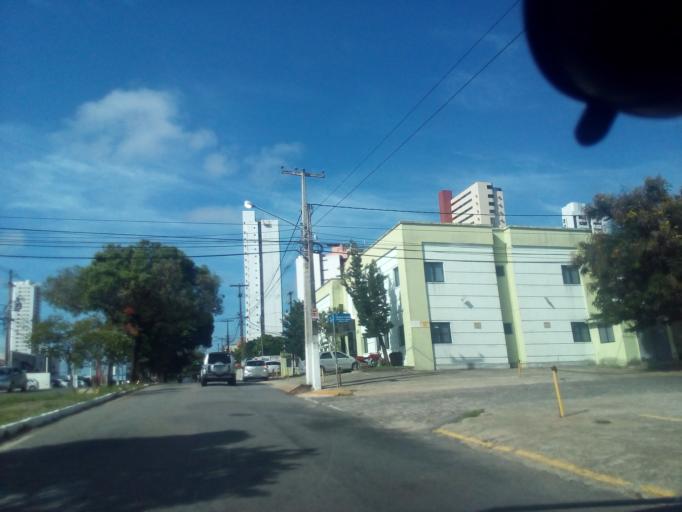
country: BR
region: Rio Grande do Norte
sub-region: Natal
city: Natal
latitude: -5.8220
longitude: -35.2161
